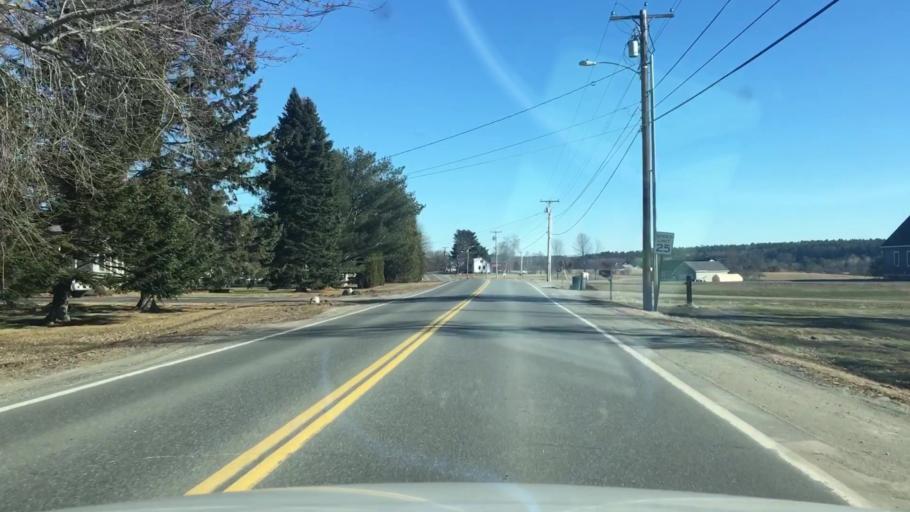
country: US
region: Maine
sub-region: Kennebec County
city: Winslow
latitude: 44.5447
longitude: -69.6037
